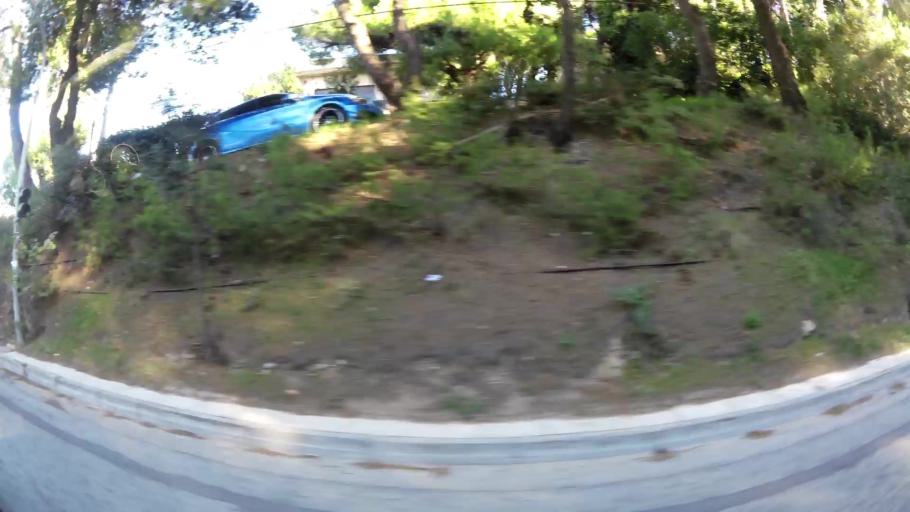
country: GR
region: Attica
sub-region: Nomarchia Anatolikis Attikis
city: Anoixi
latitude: 38.1272
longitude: 23.8568
